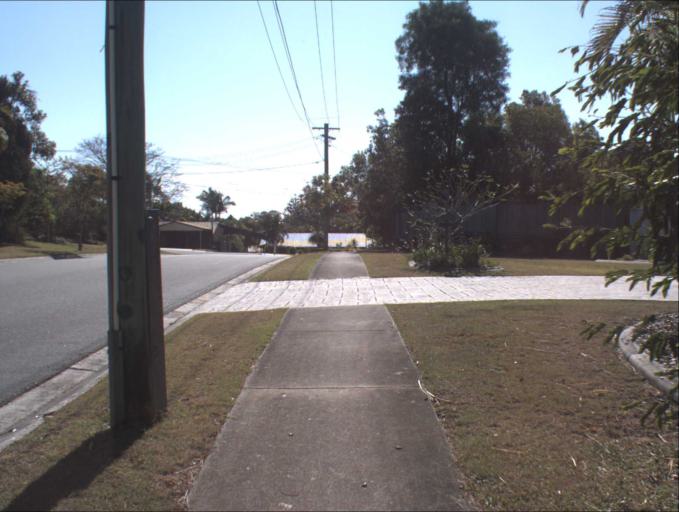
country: AU
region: Queensland
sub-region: Logan
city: Rochedale South
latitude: -27.5934
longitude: 153.1346
